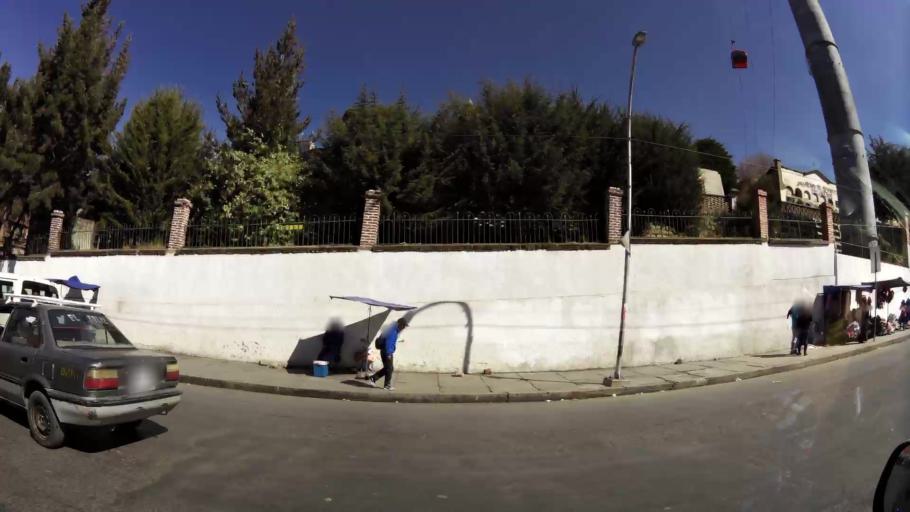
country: BO
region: La Paz
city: La Paz
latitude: -16.4958
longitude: -68.1500
